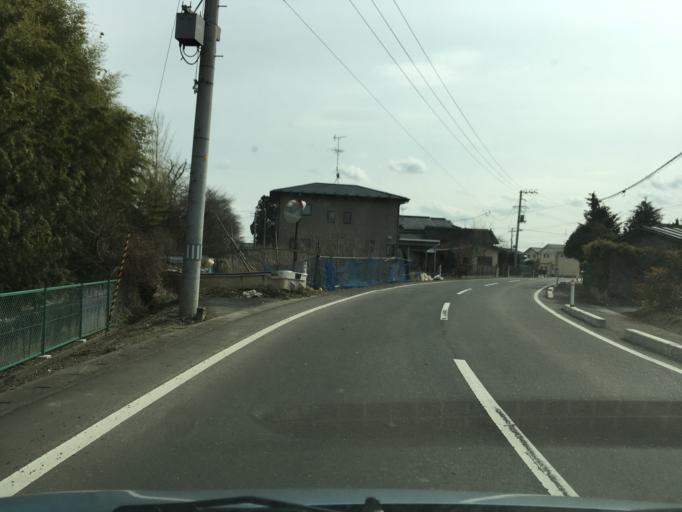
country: JP
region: Miyagi
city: Wakuya
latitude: 38.7194
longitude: 141.2429
